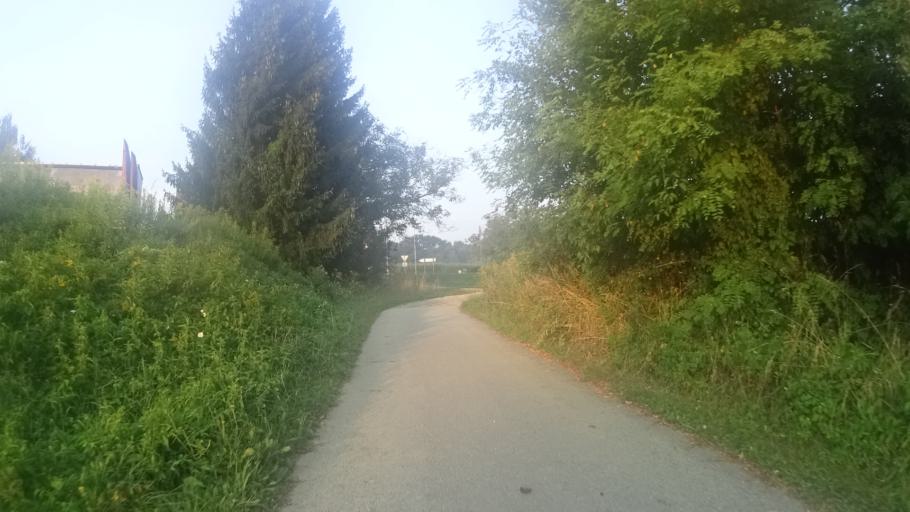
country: SI
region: Zavrc
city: Zavrc
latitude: 46.3907
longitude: 16.0508
